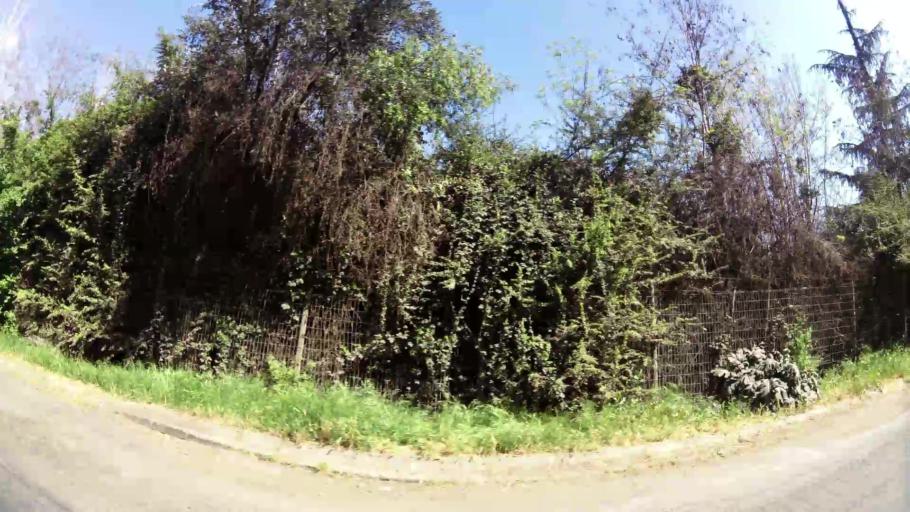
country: CL
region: Santiago Metropolitan
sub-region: Provincia de Santiago
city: Villa Presidente Frei, Nunoa, Santiago, Chile
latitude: -33.4352
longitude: -70.5182
